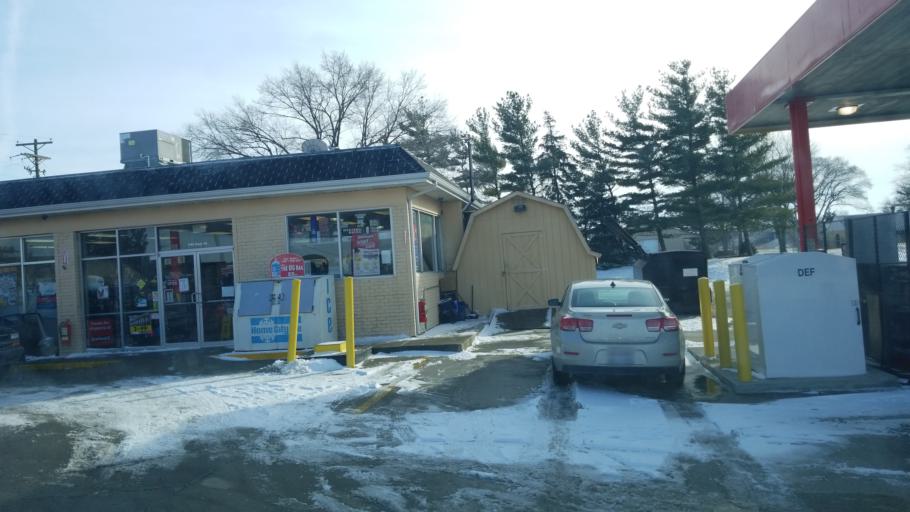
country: US
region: Ohio
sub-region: Wood County
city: North Baltimore
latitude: 41.1850
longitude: -83.6482
